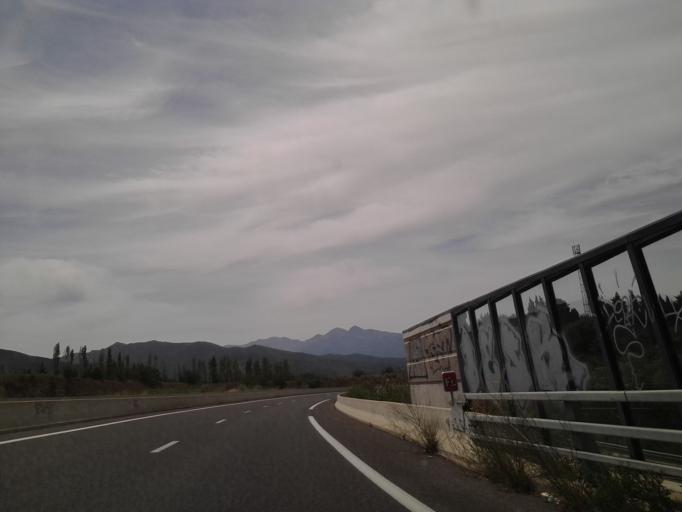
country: FR
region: Languedoc-Roussillon
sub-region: Departement des Pyrenees-Orientales
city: Ille-sur-Tet
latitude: 42.6623
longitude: 2.6021
